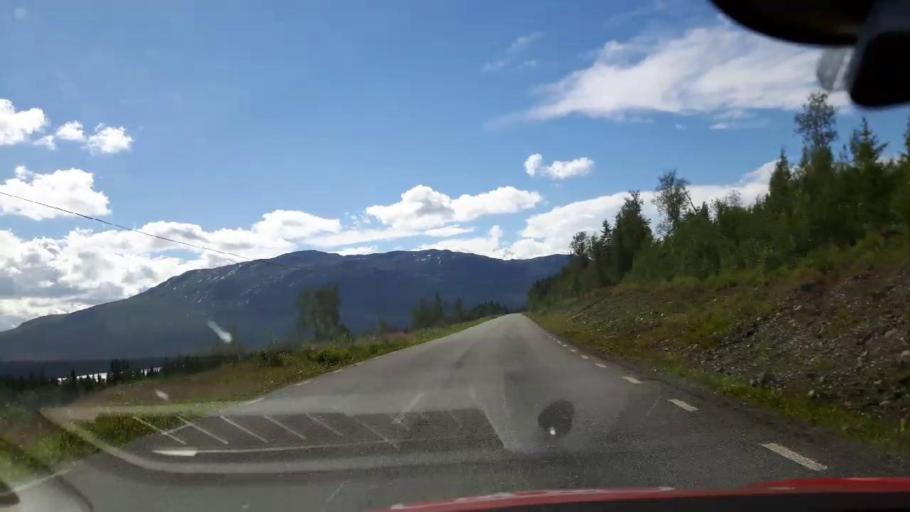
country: SE
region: Jaemtland
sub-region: Are Kommun
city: Are
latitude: 63.2179
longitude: 13.0870
